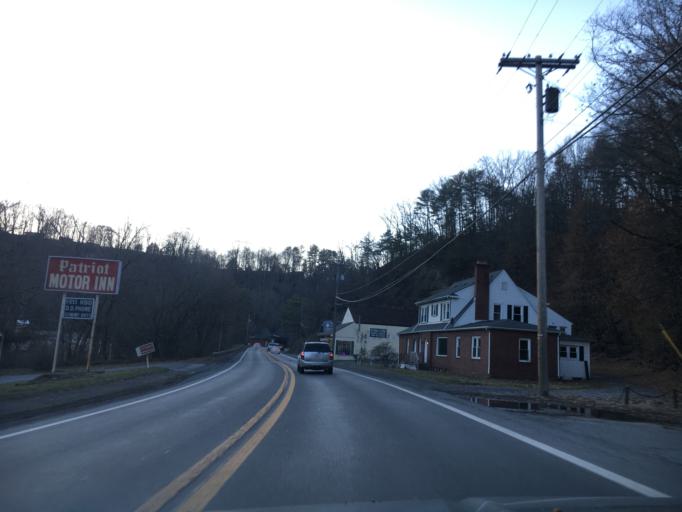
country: US
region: West Virginia
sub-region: Raleigh County
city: Beaver
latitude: 37.7514
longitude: -81.1447
